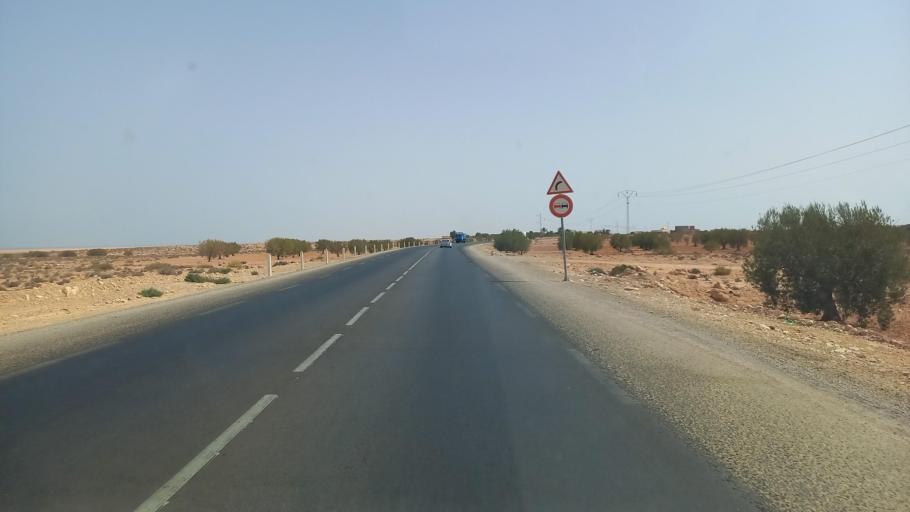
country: TN
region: Madanin
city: Medenine
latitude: 33.3877
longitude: 10.7062
